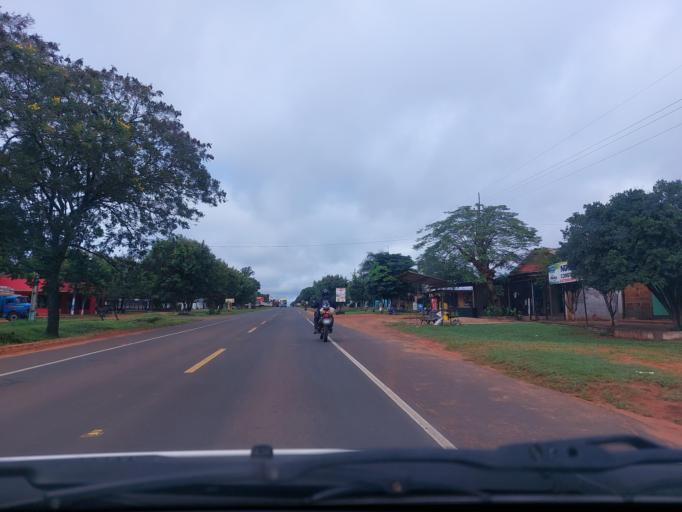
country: PY
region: San Pedro
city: Guayaybi
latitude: -24.5670
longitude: -56.4030
